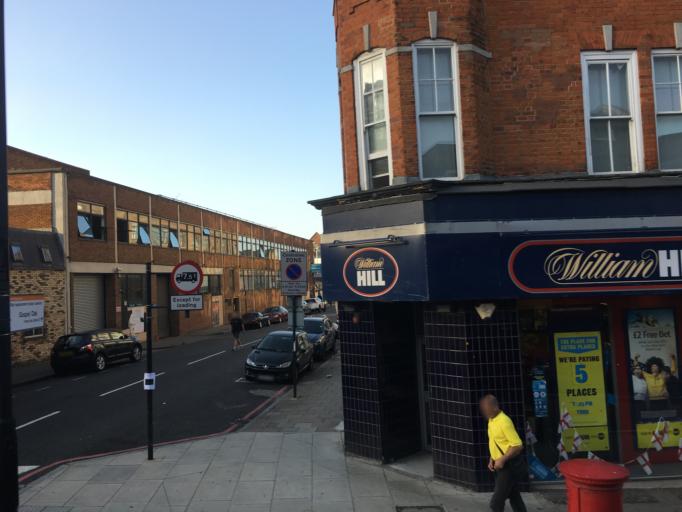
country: GB
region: England
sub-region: Greater London
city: Holloway
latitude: 51.5648
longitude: -0.1326
